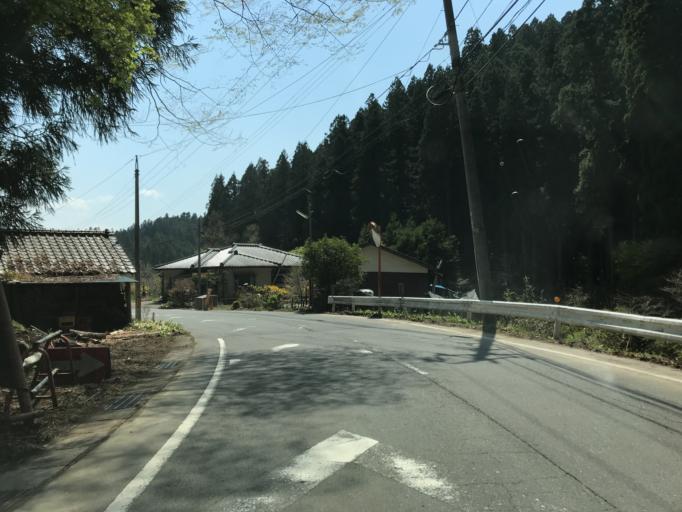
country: JP
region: Ibaraki
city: Kitaibaraki
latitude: 36.9636
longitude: 140.6655
